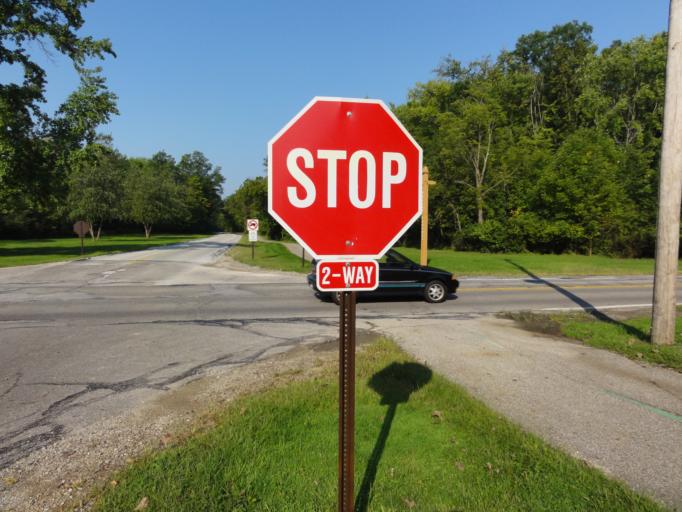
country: US
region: Ohio
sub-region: Cuyahoga County
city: North Royalton
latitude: 41.3032
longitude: -81.7541
